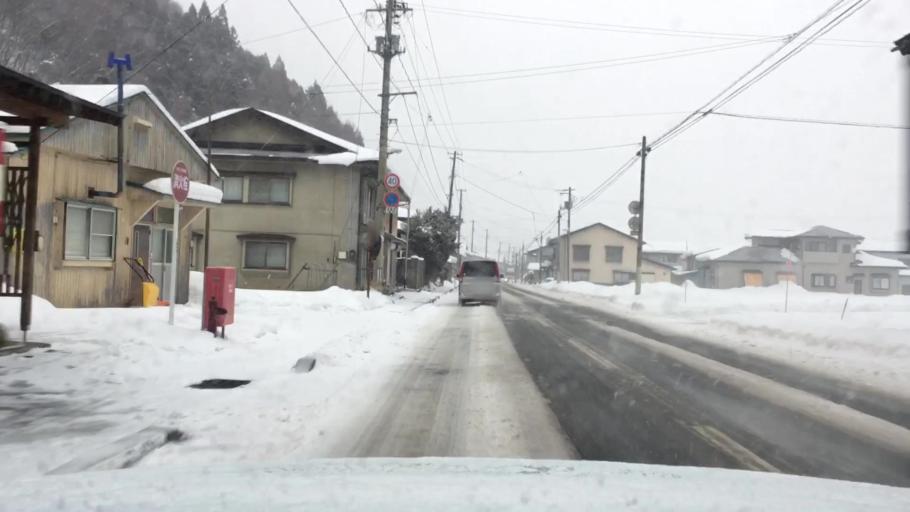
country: JP
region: Iwate
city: Ichinohe
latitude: 40.0938
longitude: 141.0470
